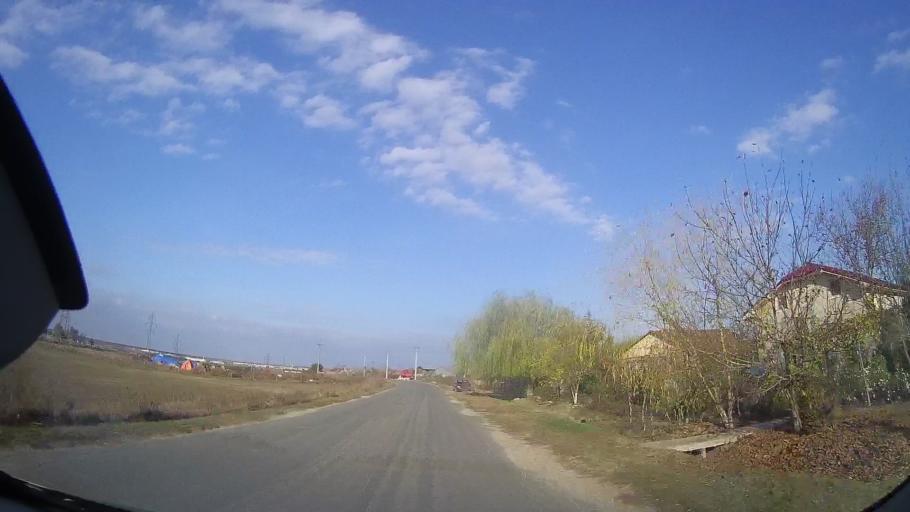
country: RO
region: Constanta
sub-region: Comuna Limanu
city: Limanu
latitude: 43.7981
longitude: 28.5209
